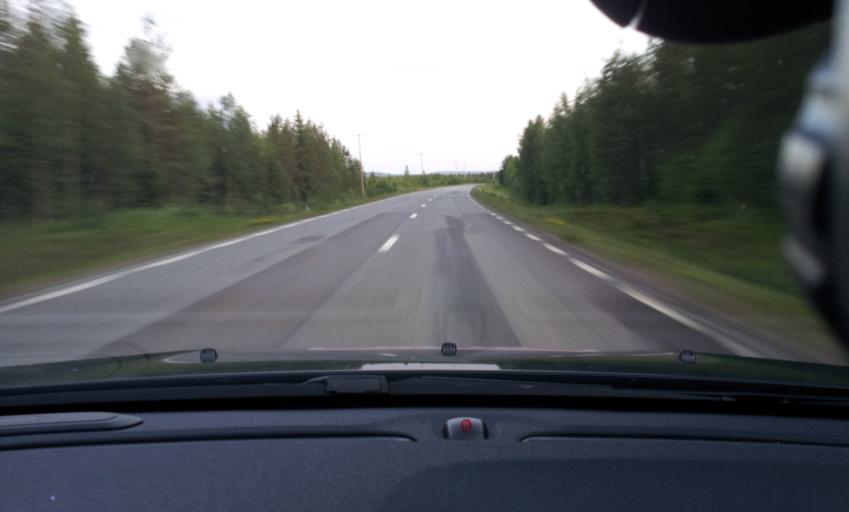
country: SE
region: Jaemtland
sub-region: Ragunda Kommun
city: Hammarstrand
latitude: 63.0005
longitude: 16.1116
